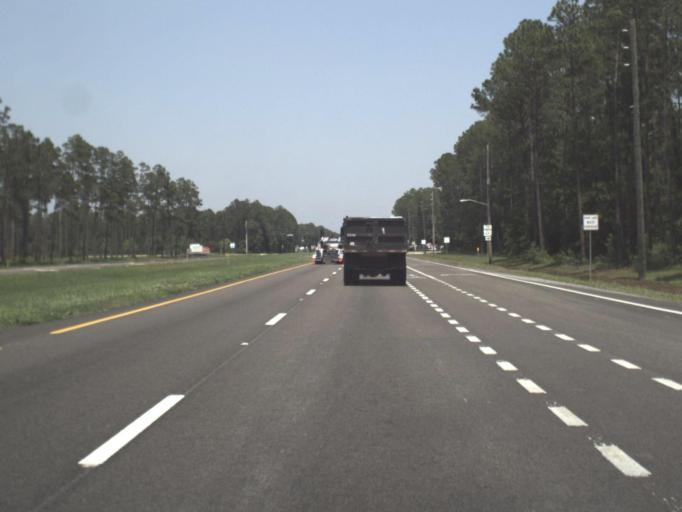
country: US
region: Florida
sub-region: Duval County
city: Baldwin
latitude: 30.2472
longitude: -81.8893
